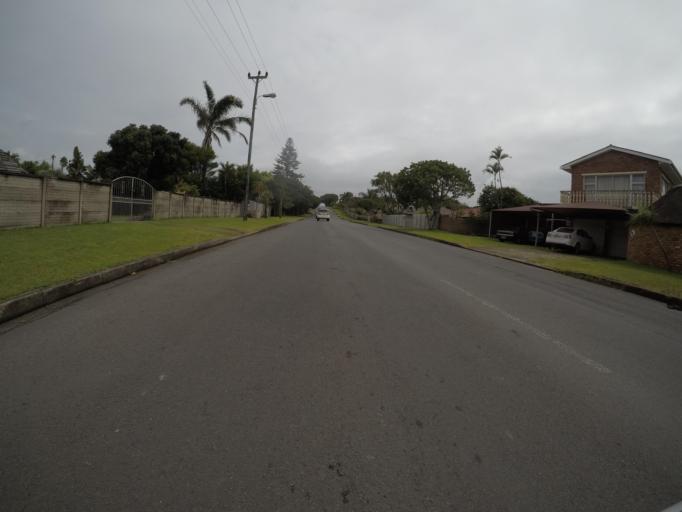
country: ZA
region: Eastern Cape
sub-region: Buffalo City Metropolitan Municipality
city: East London
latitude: -32.9434
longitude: 28.0107
